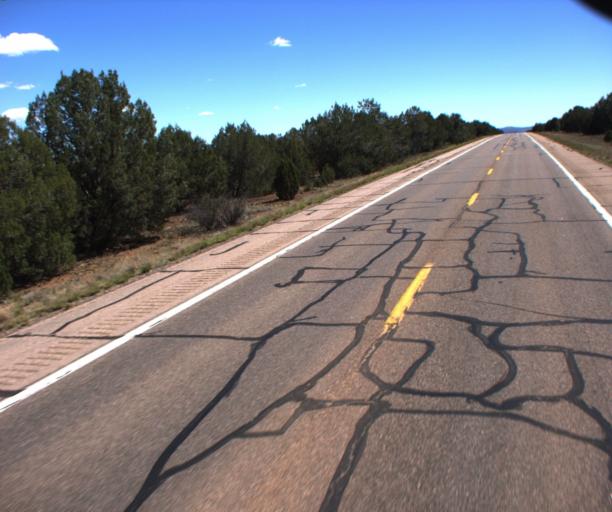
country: US
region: Arizona
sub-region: Yavapai County
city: Paulden
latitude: 35.0362
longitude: -112.3953
